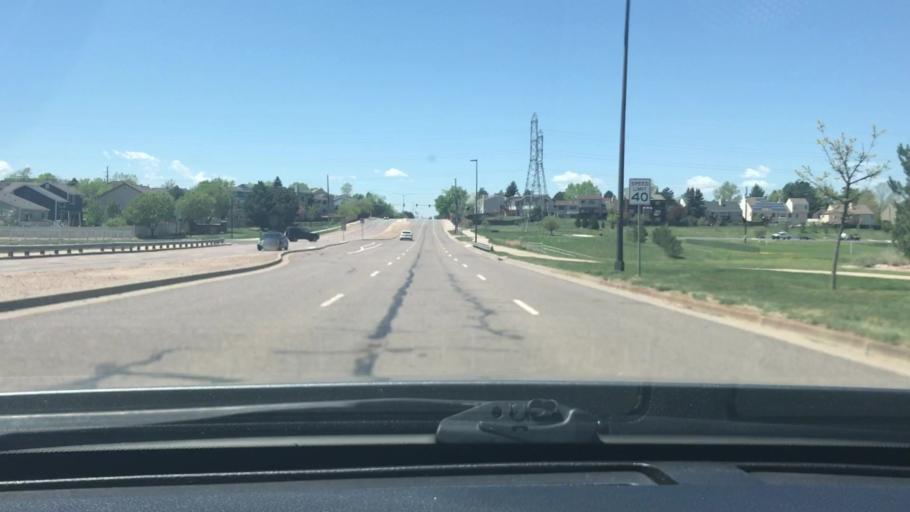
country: US
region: Colorado
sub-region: Arapahoe County
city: Dove Valley
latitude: 39.6531
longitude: -104.7512
